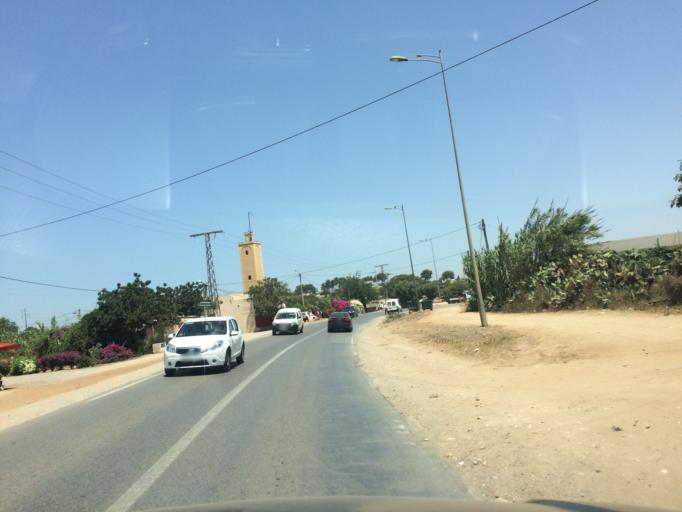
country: MA
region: Rabat-Sale-Zemmour-Zaer
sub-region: Skhirate-Temara
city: Temara
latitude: 33.8709
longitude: -6.8534
